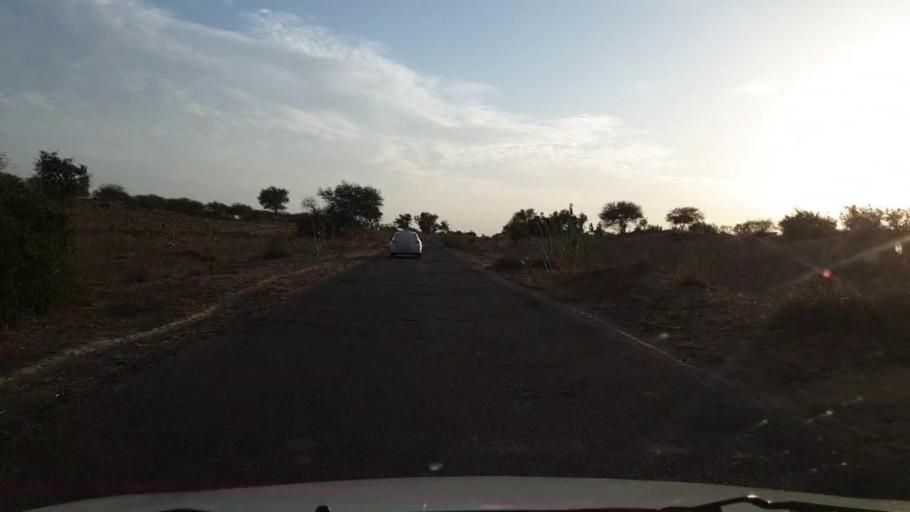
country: PK
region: Sindh
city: Nabisar
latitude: 25.0245
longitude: 69.9443
